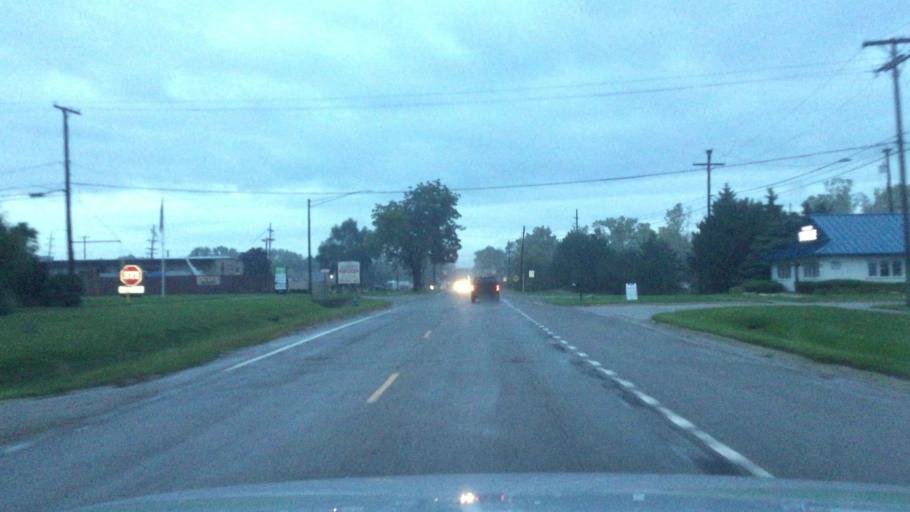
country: US
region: Michigan
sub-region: Oakland County
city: Waterford
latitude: 42.6924
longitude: -83.4075
